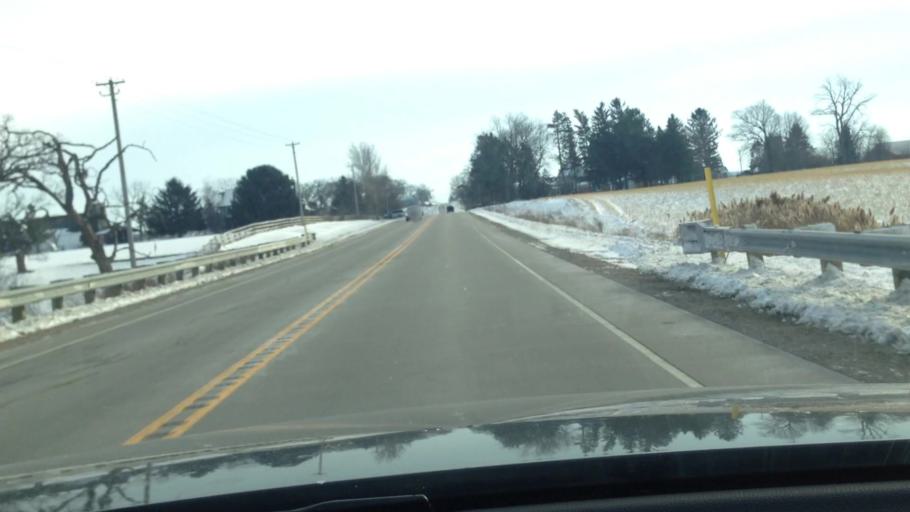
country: US
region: Wisconsin
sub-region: Walworth County
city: Lake Geneva
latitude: 42.5370
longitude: -88.4429
